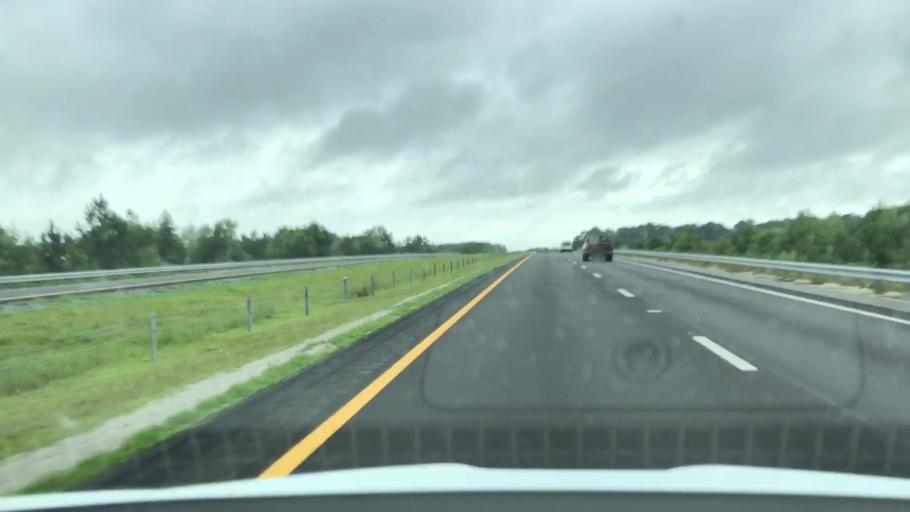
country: US
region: North Carolina
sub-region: Wayne County
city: Fremont
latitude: 35.4664
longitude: -77.9861
